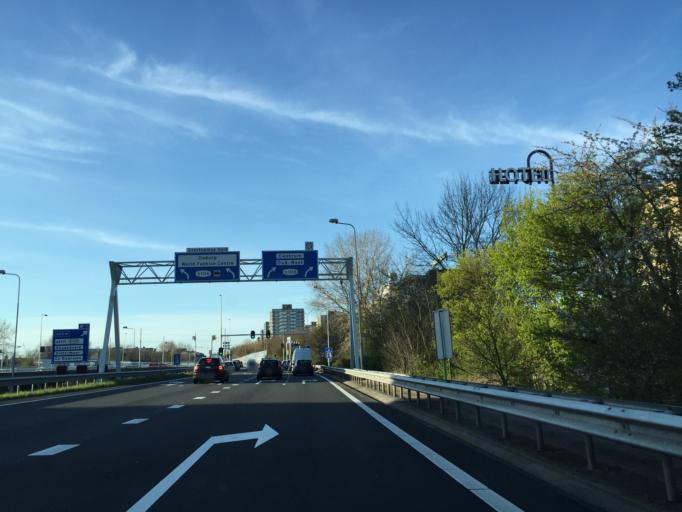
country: NL
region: North Holland
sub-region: Gemeente Amsterdam
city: Amsterdam
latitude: 52.3567
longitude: 4.8430
